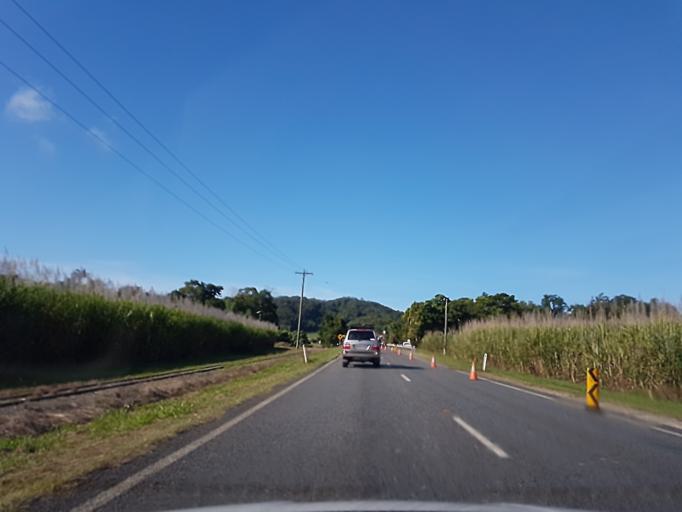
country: AU
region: Queensland
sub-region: Cairns
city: Port Douglas
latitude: -16.3922
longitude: 145.3919
